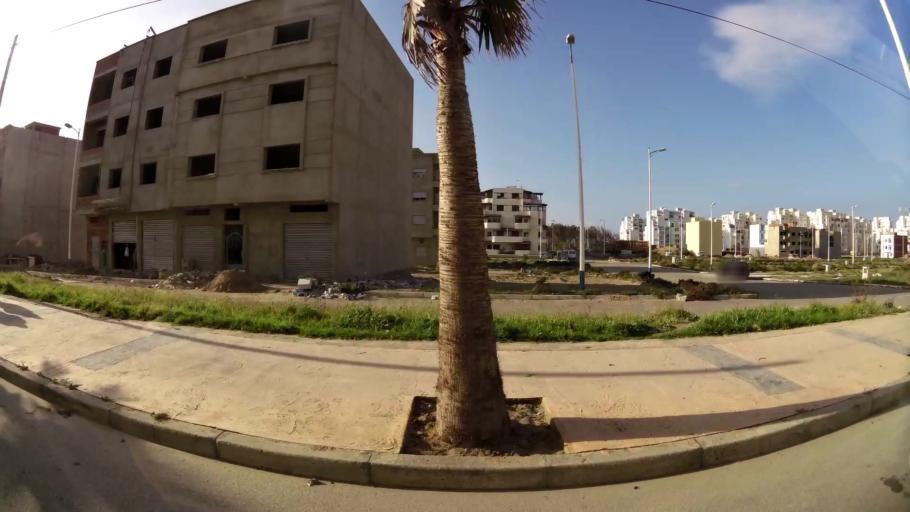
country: MA
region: Tanger-Tetouan
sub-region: Tetouan
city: Martil
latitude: 35.6289
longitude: -5.2782
